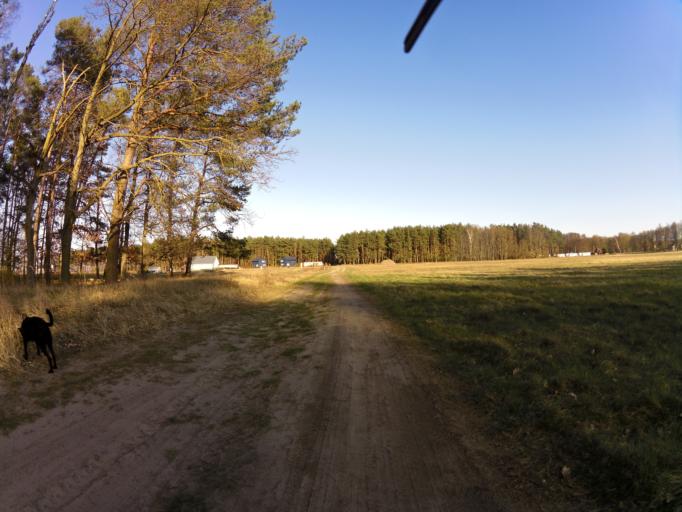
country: PL
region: West Pomeranian Voivodeship
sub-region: Powiat policki
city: Nowe Warpno
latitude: 53.7332
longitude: 14.3211
